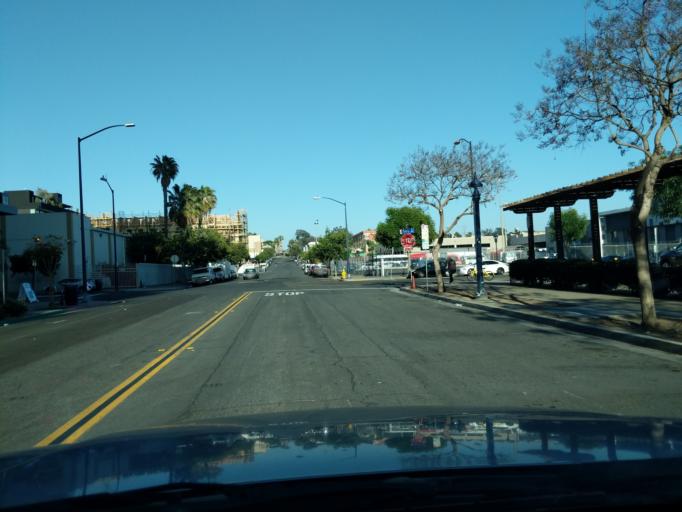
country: US
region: California
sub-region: San Diego County
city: San Diego
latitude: 32.7084
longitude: -117.1524
